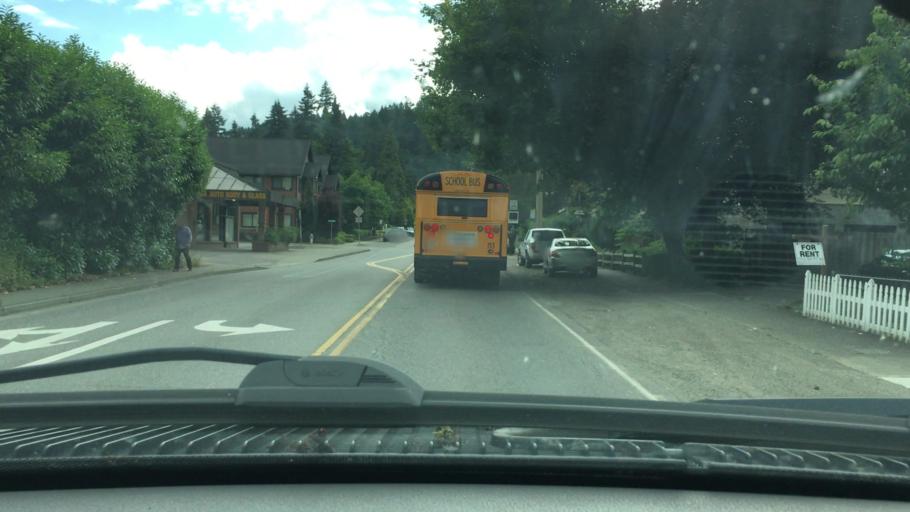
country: US
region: Washington
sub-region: King County
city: Issaquah
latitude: 47.5301
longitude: -122.0322
